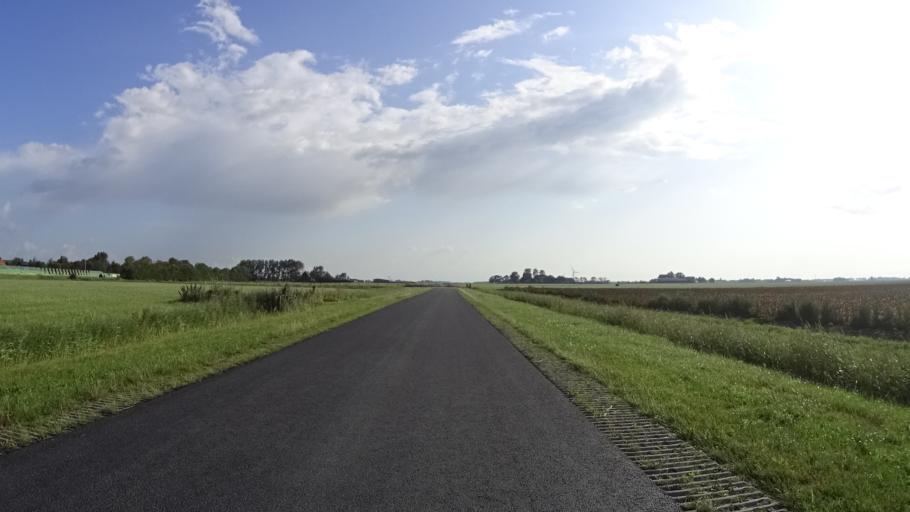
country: NL
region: Friesland
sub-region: Sudwest Fryslan
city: Makkum
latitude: 53.1083
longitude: 5.3953
